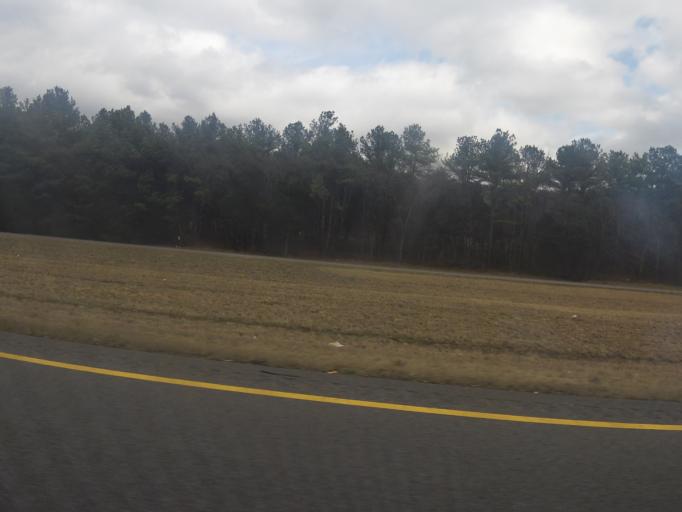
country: US
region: Tennessee
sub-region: Rutherford County
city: Plainview
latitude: 35.6592
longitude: -86.2683
